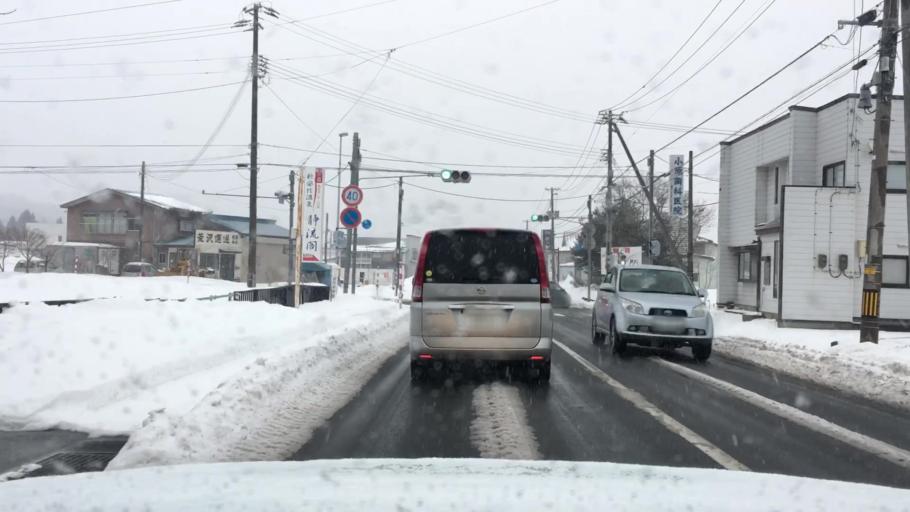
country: JP
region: Iwate
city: Ichinohe
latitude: 40.1048
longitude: 141.0497
